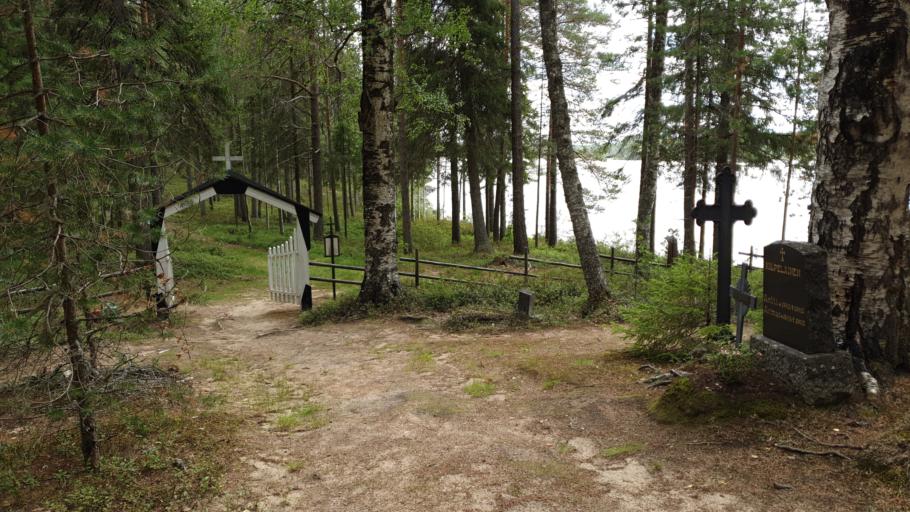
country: FI
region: Kainuu
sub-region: Kehys-Kainuu
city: Kuhmo
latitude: 64.3826
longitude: 29.8021
